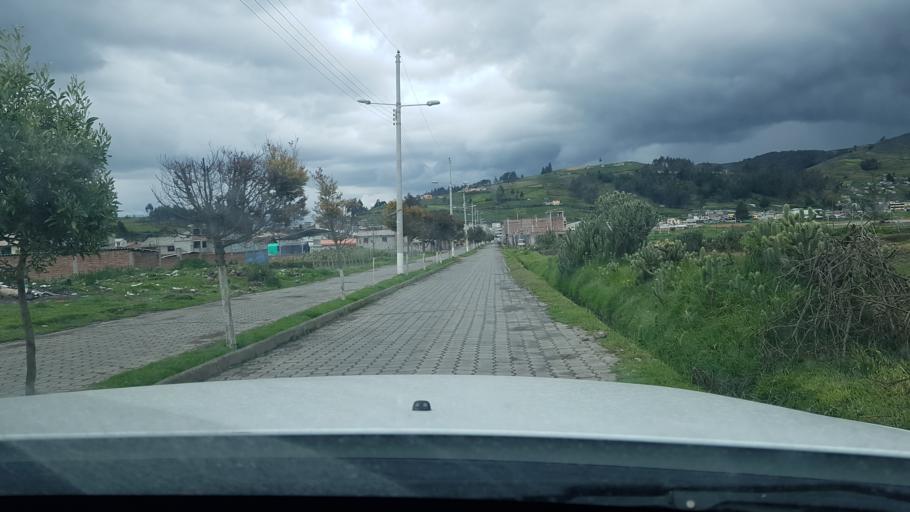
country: EC
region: Chimborazo
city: Riobamba
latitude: -1.7054
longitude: -78.7762
